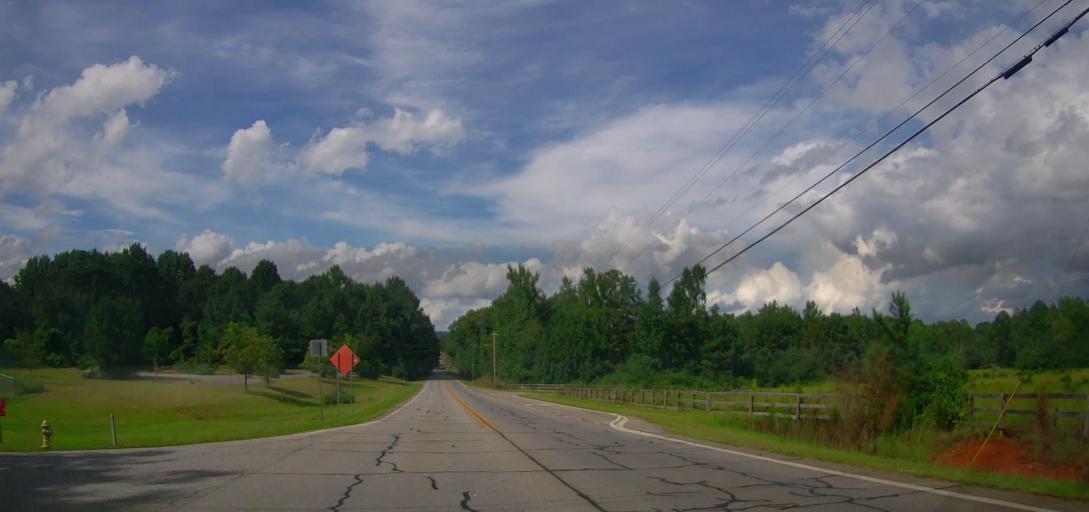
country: US
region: Georgia
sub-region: Harris County
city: Hamilton
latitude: 32.7631
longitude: -84.8750
